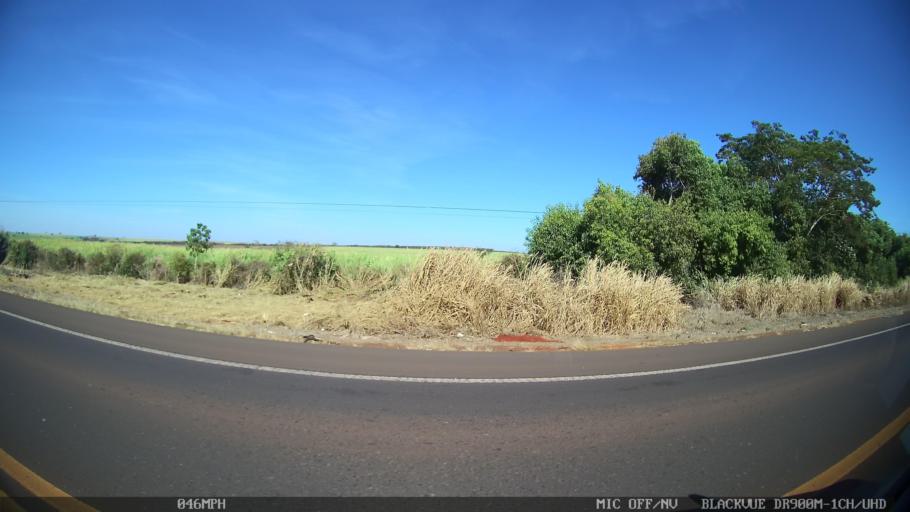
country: BR
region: Sao Paulo
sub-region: Barretos
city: Barretos
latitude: -20.5724
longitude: -48.6738
